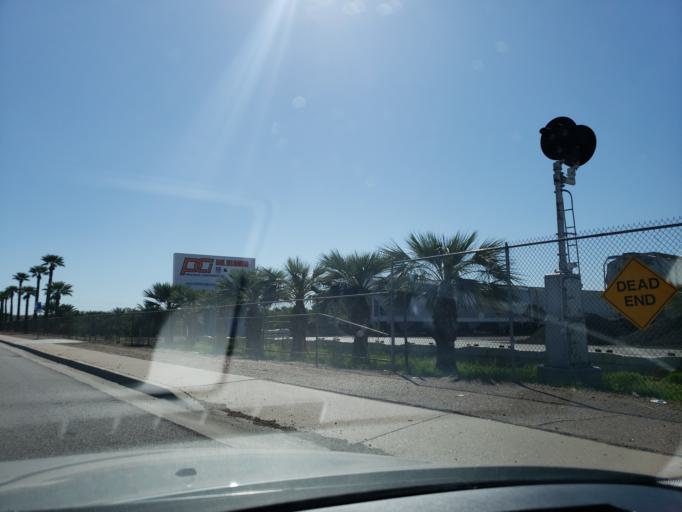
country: US
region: Arizona
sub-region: Maricopa County
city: Phoenix
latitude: 33.4367
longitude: -112.1389
